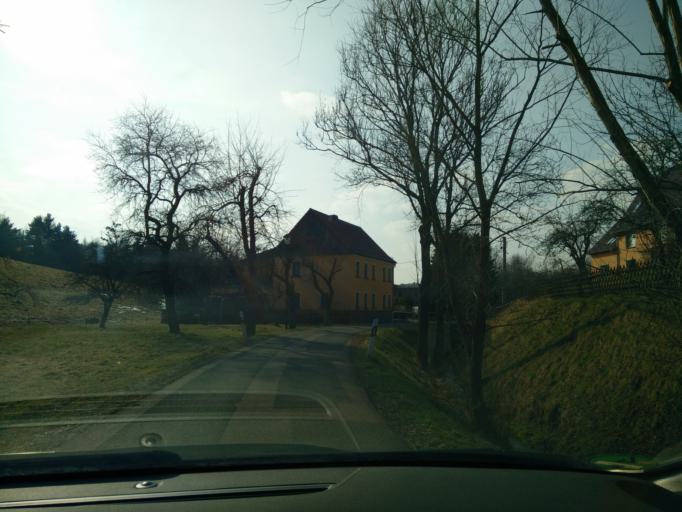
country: DE
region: Saxony
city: Geringswalde
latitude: 51.1108
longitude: 12.8653
